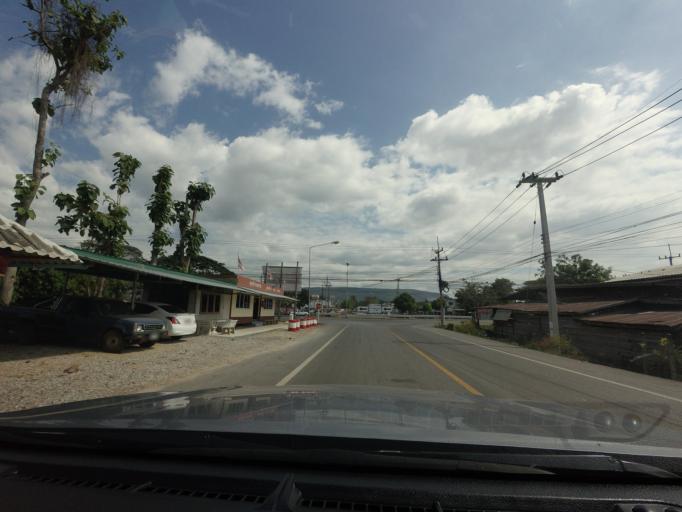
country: TH
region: Phitsanulok
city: Wang Thong
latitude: 16.7406
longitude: 100.4313
